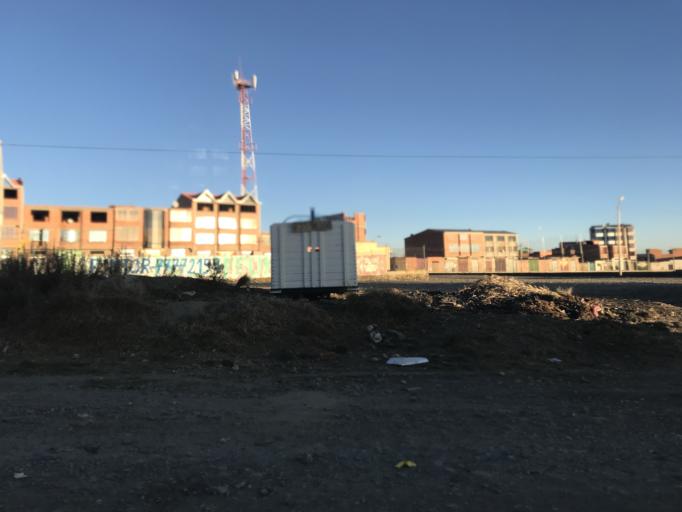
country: BO
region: La Paz
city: La Paz
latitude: -16.5001
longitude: -68.2356
